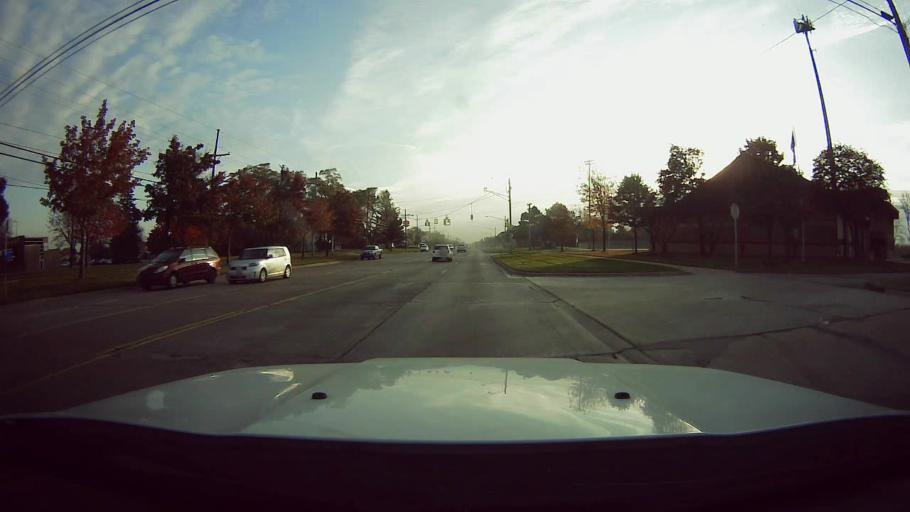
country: US
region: Michigan
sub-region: Macomb County
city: Sterling Heights
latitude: 42.5520
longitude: -82.9954
